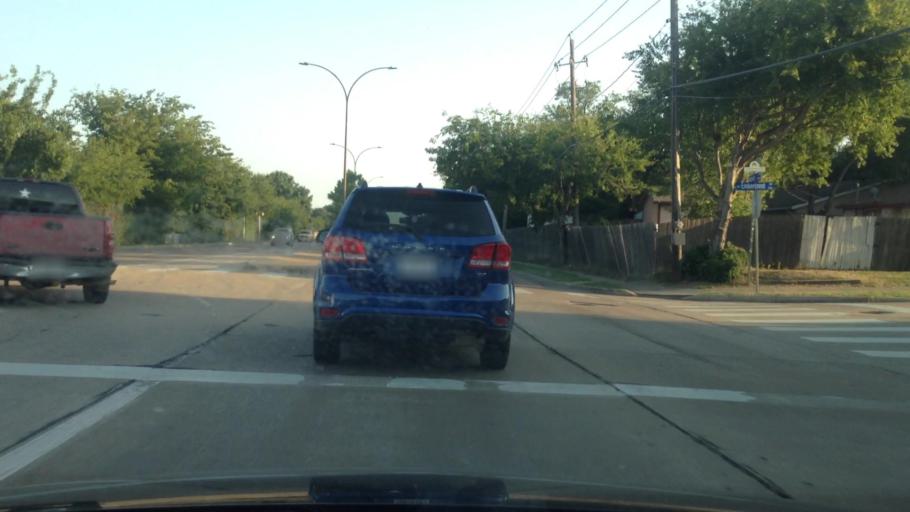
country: US
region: Texas
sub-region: Tarrant County
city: Dalworthington Gardens
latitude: 32.6680
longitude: -97.1150
